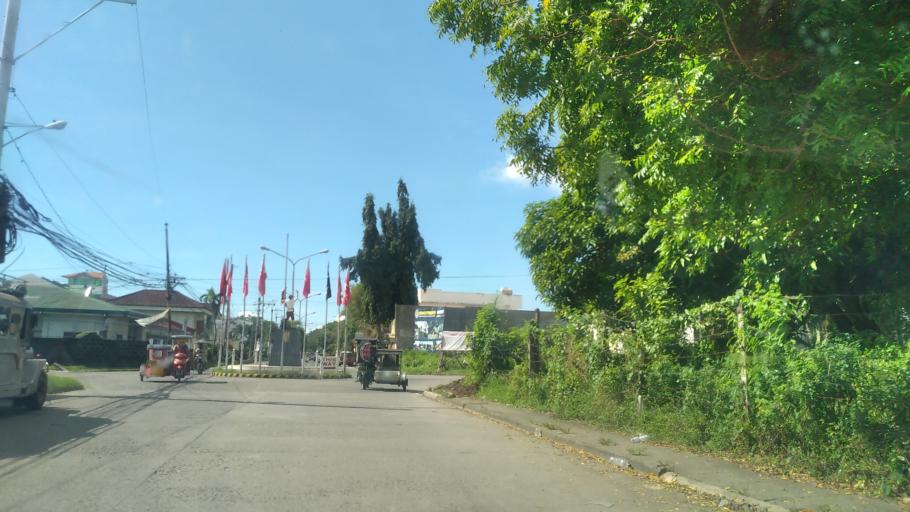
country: PH
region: Calabarzon
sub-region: Province of Quezon
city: Lucena
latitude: 13.9411
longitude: 121.6036
